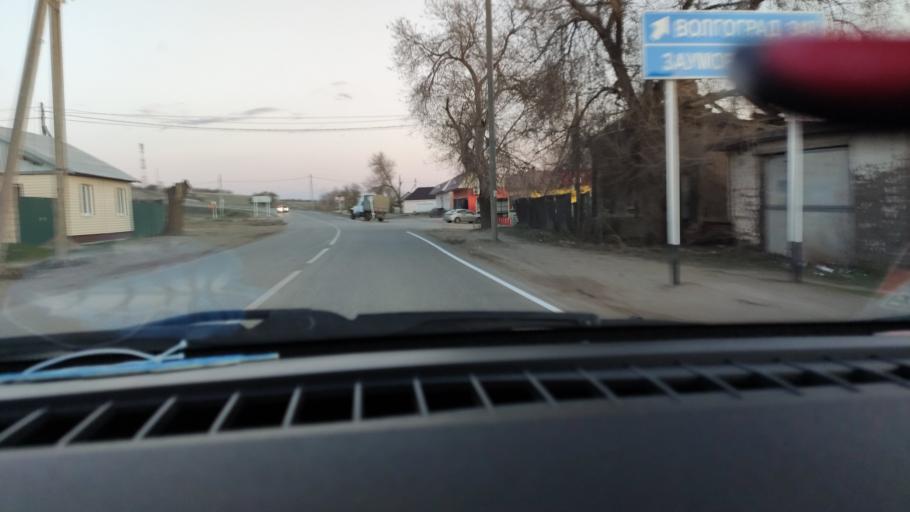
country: RU
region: Saratov
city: Privolzhskiy
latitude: 51.1798
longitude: 45.9219
